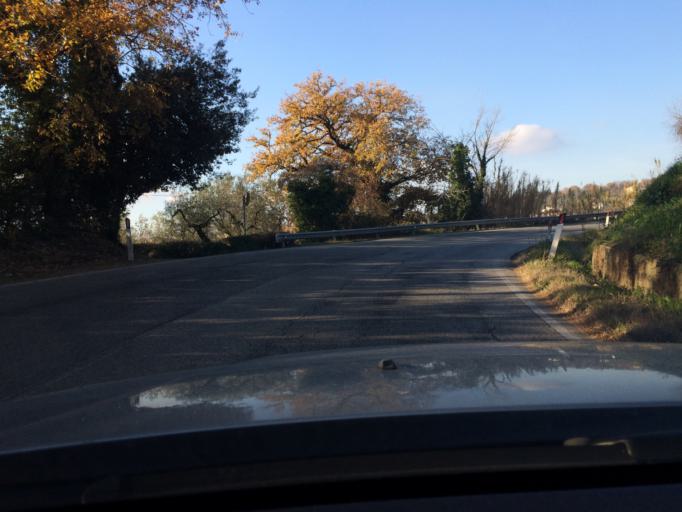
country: IT
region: Umbria
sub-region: Provincia di Terni
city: Fornole
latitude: 42.5524
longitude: 12.4424
